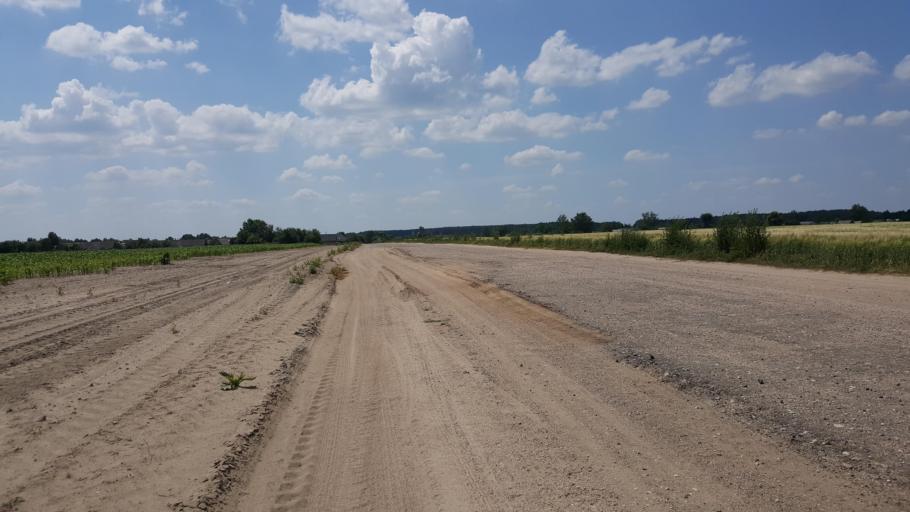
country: BY
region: Brest
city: Kamyanyets
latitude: 52.4010
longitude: 23.7634
